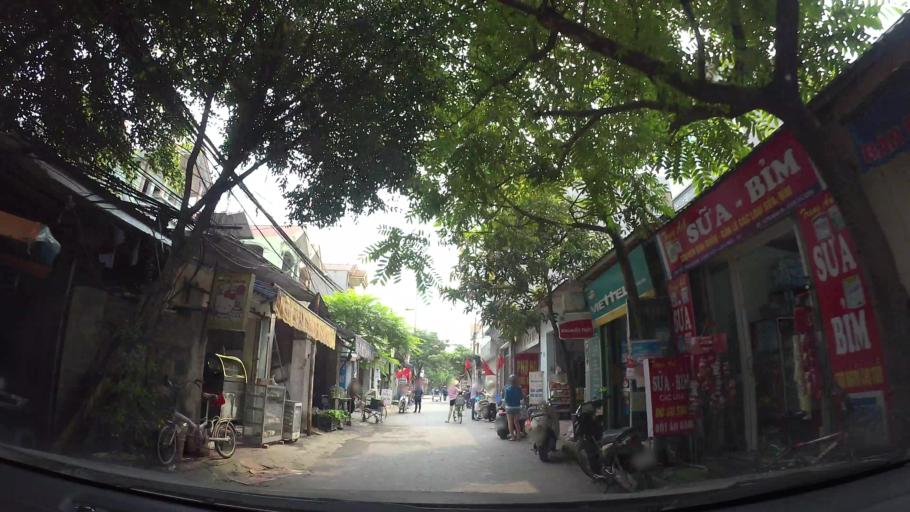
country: VN
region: Ha Noi
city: Trau Quy
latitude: 21.0720
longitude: 105.9166
